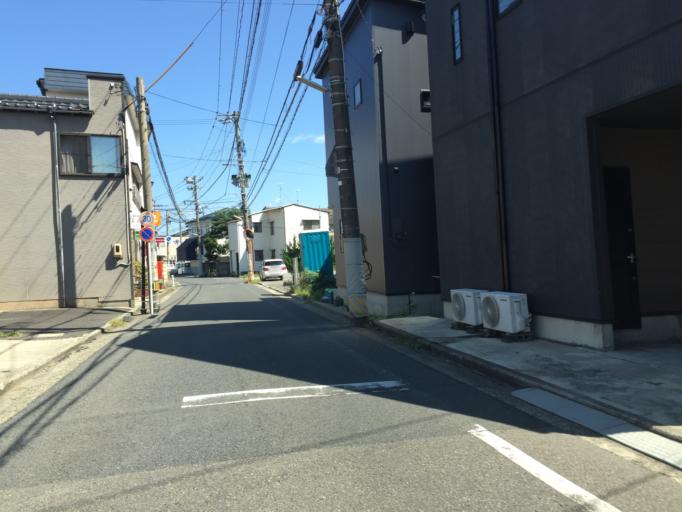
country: JP
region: Niigata
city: Niigata-shi
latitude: 37.9278
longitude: 139.0401
